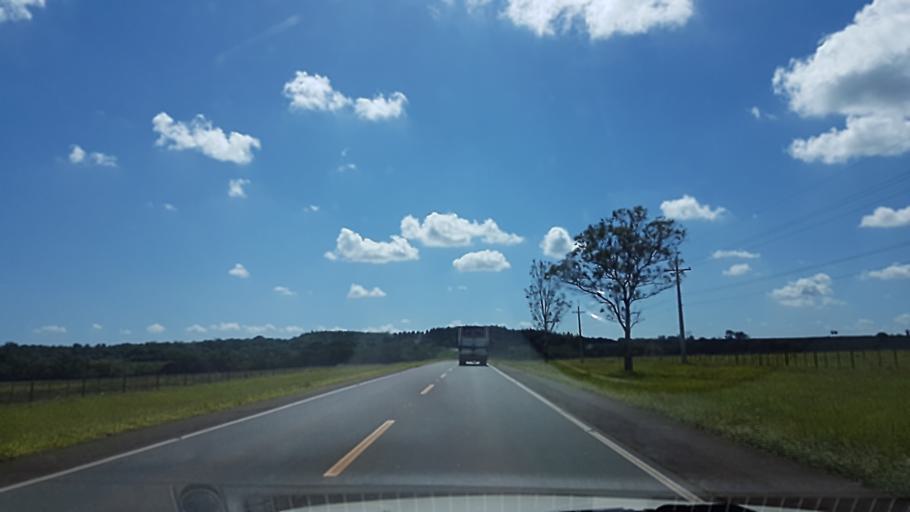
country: PY
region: Itapua
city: Carmen del Parana
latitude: -27.2208
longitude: -56.1066
